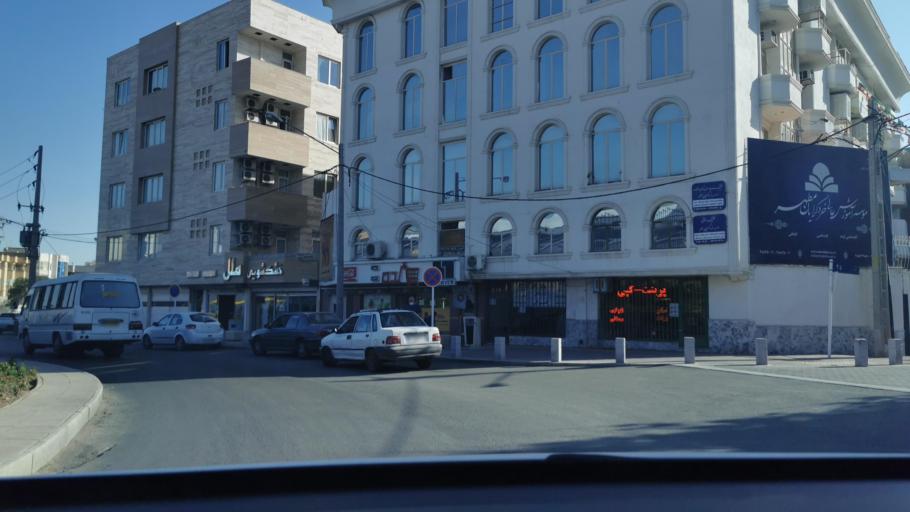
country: IR
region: Razavi Khorasan
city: Mashhad
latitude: 36.3109
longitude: 59.5135
